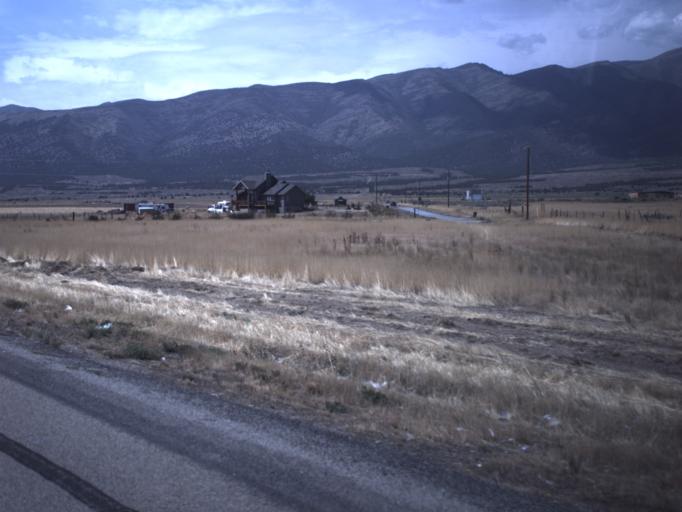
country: US
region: Utah
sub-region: Utah County
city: Eagle Mountain
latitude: 40.3476
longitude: -112.0772
